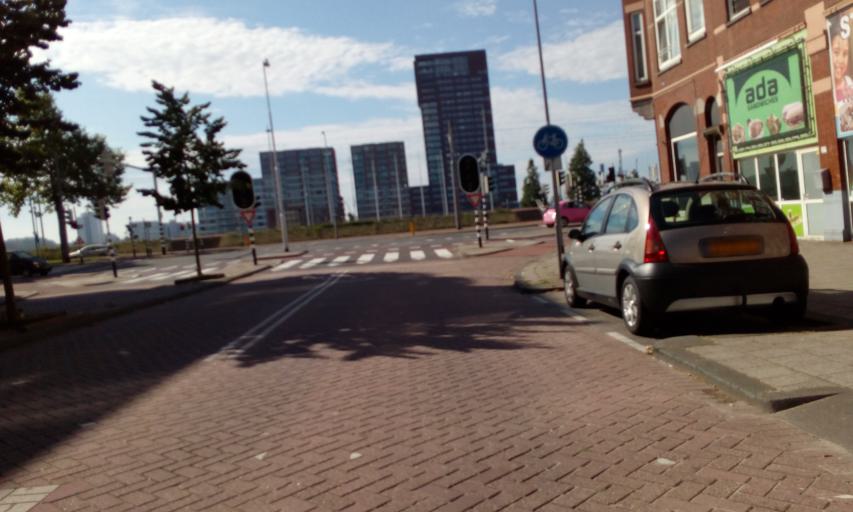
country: NL
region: South Holland
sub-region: Gemeente Rotterdam
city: Delfshaven
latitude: 51.9043
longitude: 4.4538
